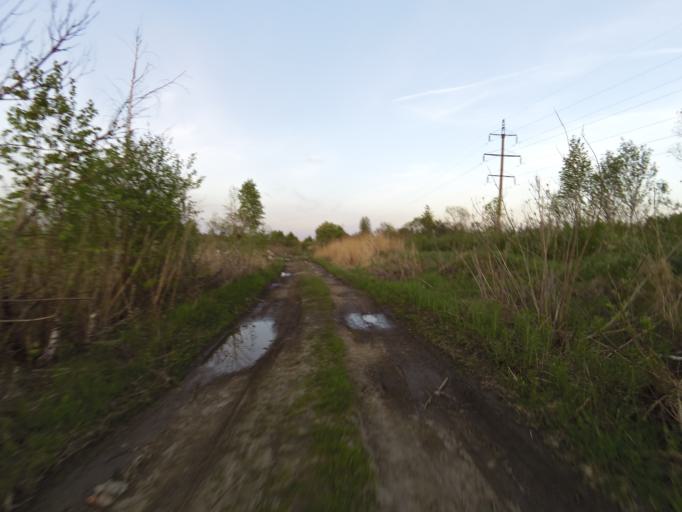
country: RU
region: Sverdlovsk
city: Shirokaya Rechka
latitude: 56.8397
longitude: 60.5086
